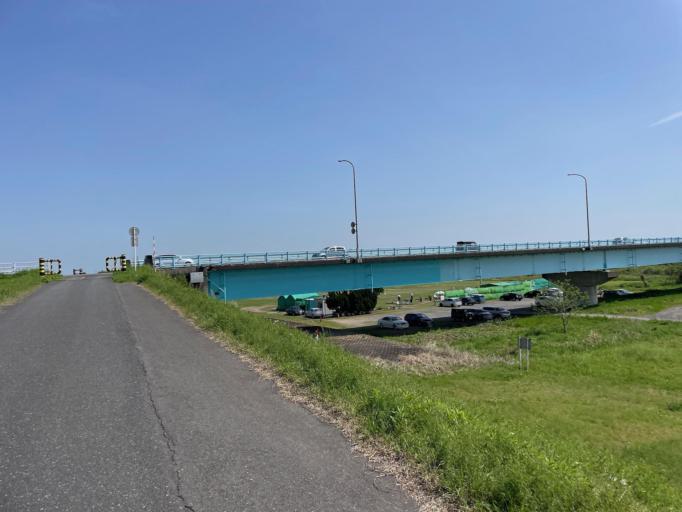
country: JP
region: Tochigi
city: Ashikaga
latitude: 36.3044
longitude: 139.4998
